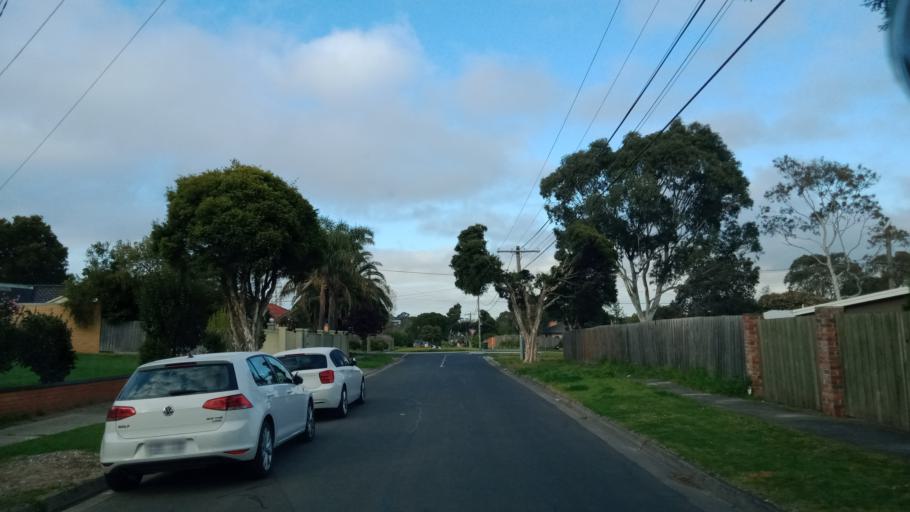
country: AU
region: Victoria
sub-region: Monash
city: Notting Hill
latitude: -37.8887
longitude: 145.1372
